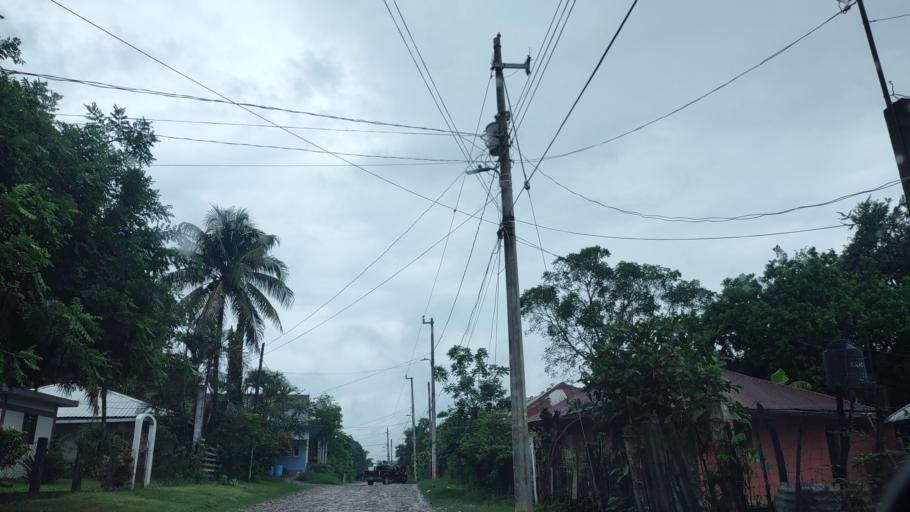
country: MX
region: San Luis Potosi
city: Tanquian de Escobedo
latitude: 21.5431
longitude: -98.5522
